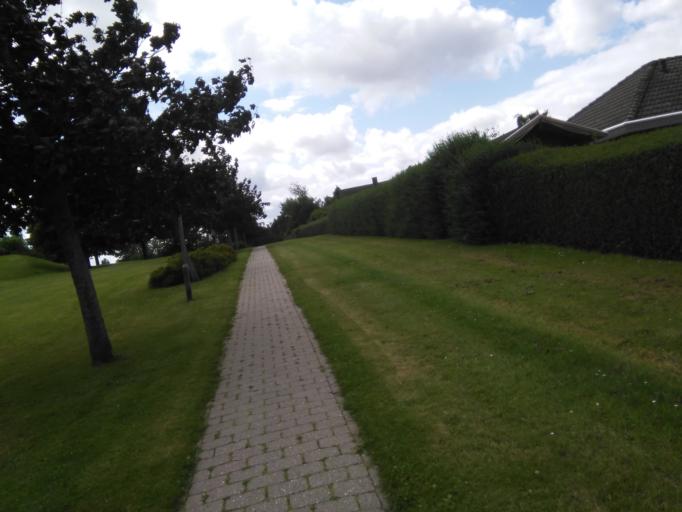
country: DK
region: Central Jutland
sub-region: Arhus Kommune
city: Marslet
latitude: 56.0741
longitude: 10.1530
